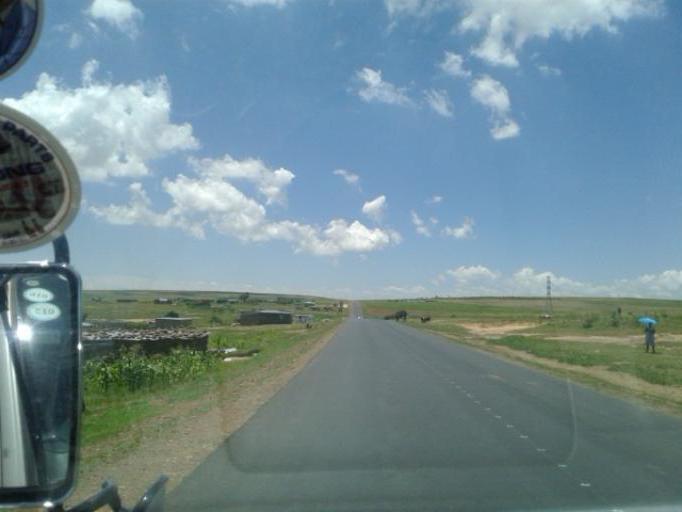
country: LS
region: Maseru
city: Maseru
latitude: -29.3148
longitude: 27.5918
